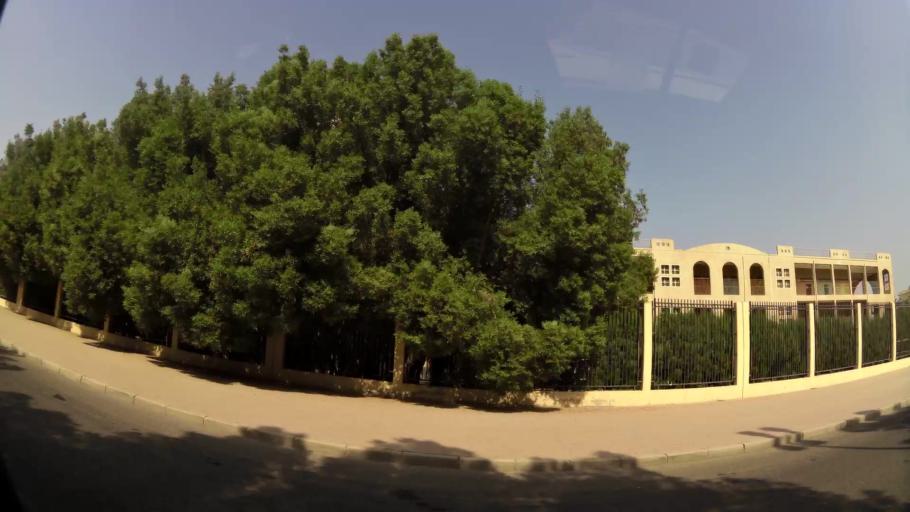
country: KW
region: Al Asimah
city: Ad Dasmah
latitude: 29.3507
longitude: 48.0171
